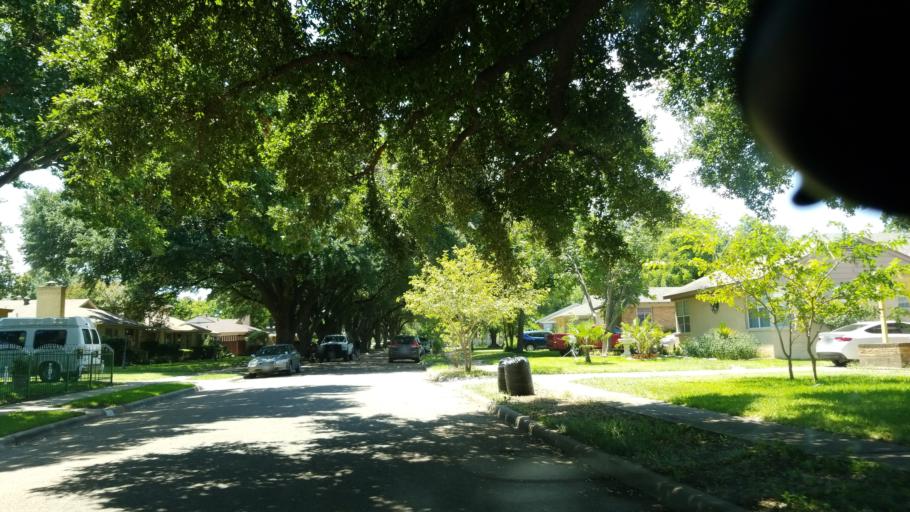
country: US
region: Texas
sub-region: Dallas County
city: Cockrell Hill
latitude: 32.7167
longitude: -96.8439
